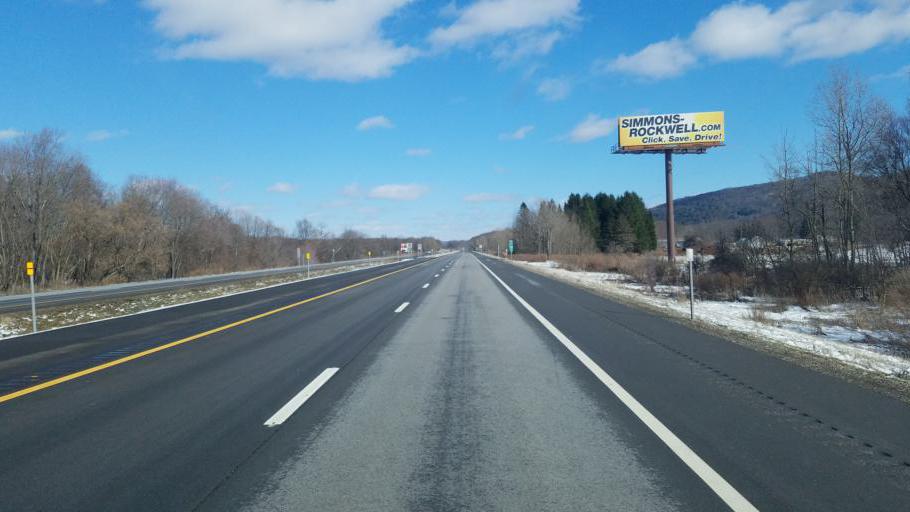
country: US
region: New York
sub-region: Cattaraugus County
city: Allegany
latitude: 42.0857
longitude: -78.5999
